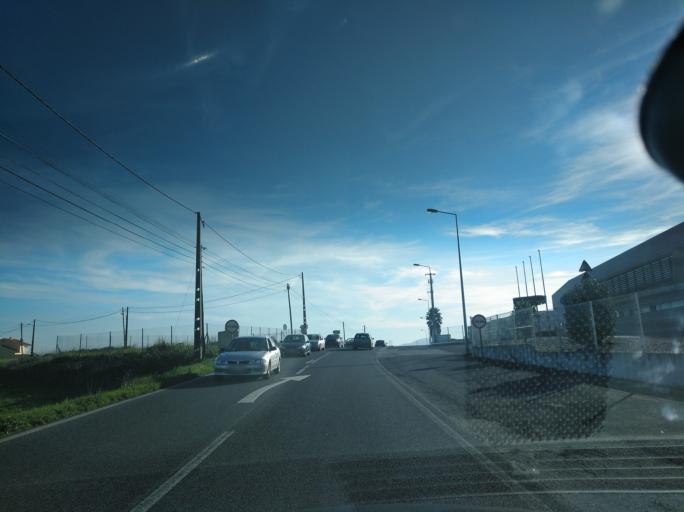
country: PT
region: Lisbon
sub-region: Mafra
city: Mafra
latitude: 38.9125
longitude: -9.3274
